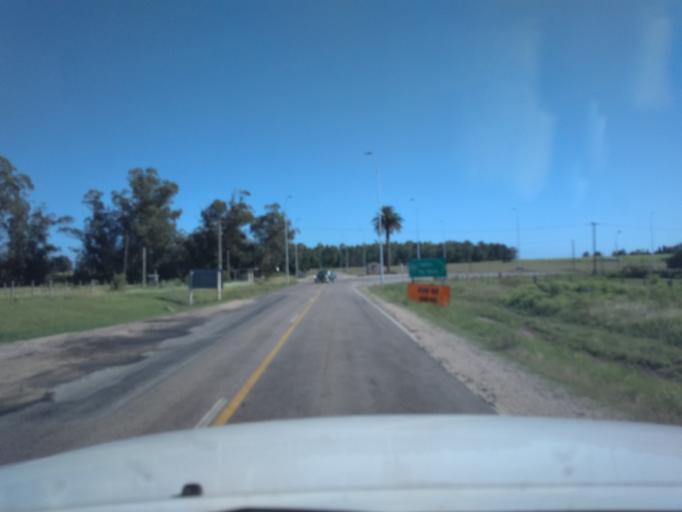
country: UY
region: Canelones
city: San Ramon
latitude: -34.2440
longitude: -55.9254
